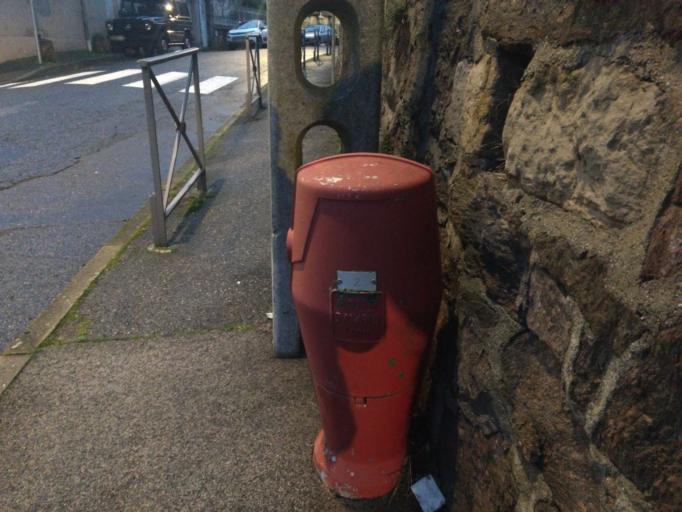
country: FR
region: Midi-Pyrenees
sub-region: Departement de l'Aveyron
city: Le Monastere
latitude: 44.3443
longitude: 2.5730
